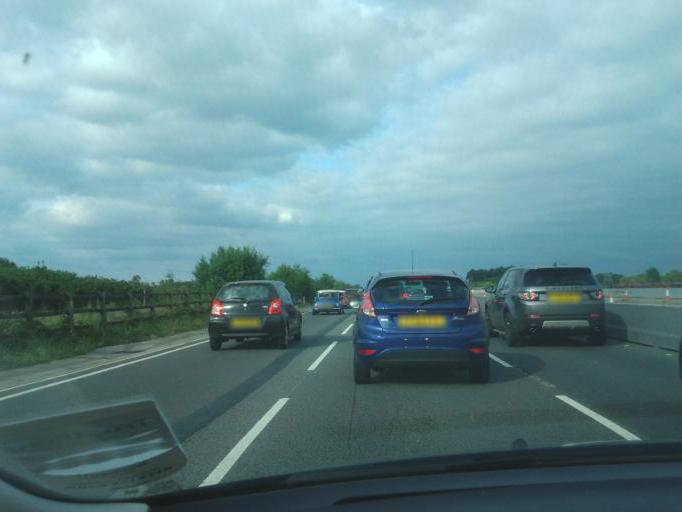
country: GB
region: England
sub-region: Surrey
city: Chobham
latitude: 51.3724
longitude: -0.6129
